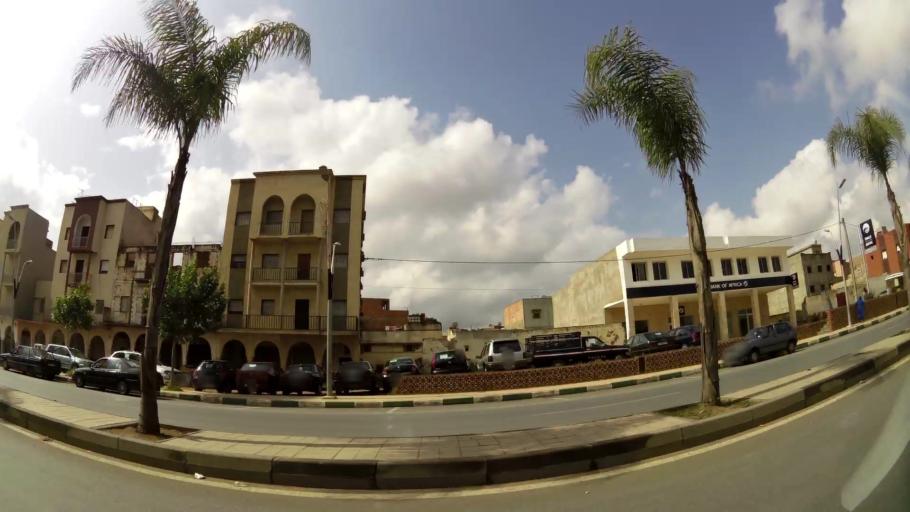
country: MA
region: Rabat-Sale-Zemmour-Zaer
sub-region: Khemisset
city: Tiflet
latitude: 33.8933
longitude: -6.3192
